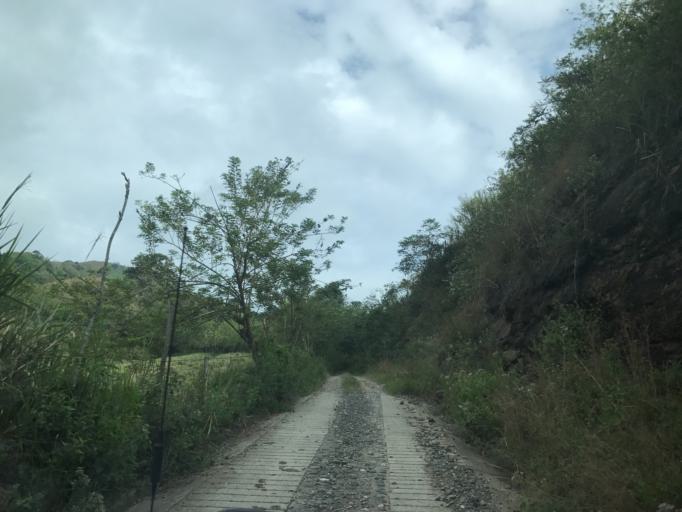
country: CO
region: Valle del Cauca
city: Obando
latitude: 4.5533
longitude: -75.8786
